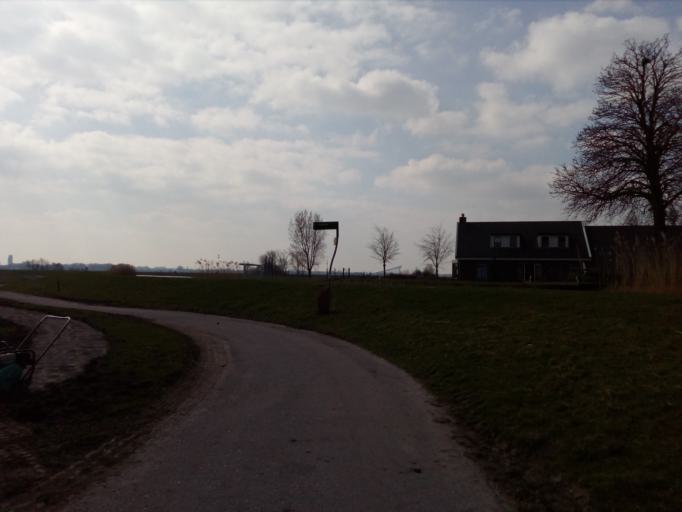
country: NL
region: South Holland
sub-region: Gemeente Zoetermeer
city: Zoetermeer
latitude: 52.0916
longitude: 4.5003
